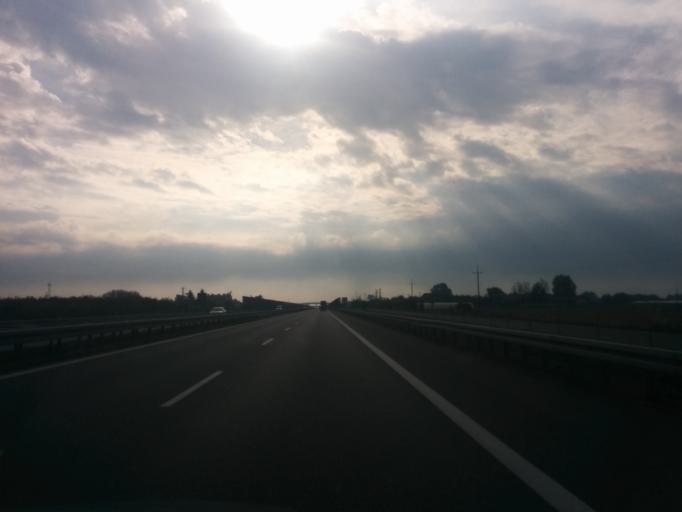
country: PL
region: Masovian Voivodeship
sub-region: Powiat bialobrzeski
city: Stara Blotnica
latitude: 51.5533
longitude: 21.0378
